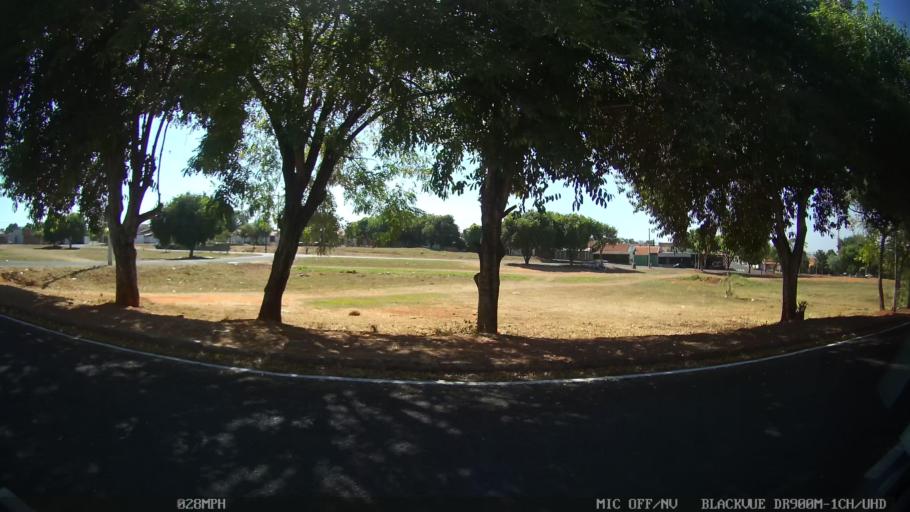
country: BR
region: Sao Paulo
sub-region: Sao Jose Do Rio Preto
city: Sao Jose do Rio Preto
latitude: -20.7737
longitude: -49.4123
